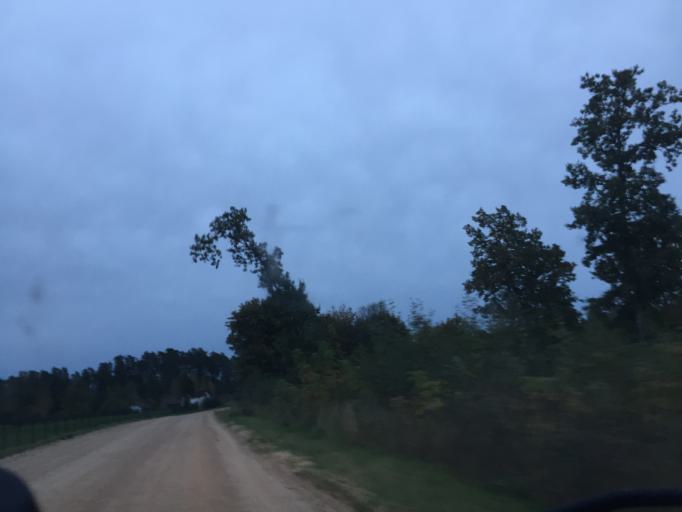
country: LV
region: Adazi
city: Adazi
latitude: 57.0842
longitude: 24.3582
